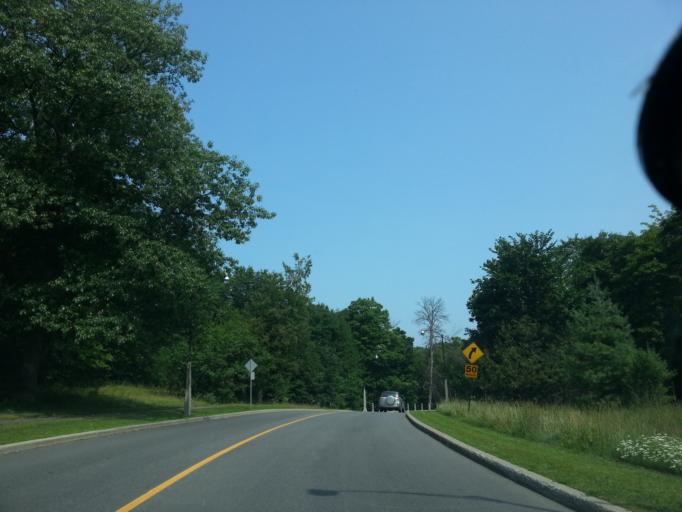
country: CA
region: Quebec
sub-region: Outaouais
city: Gatineau
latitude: 45.4476
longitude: -75.6889
